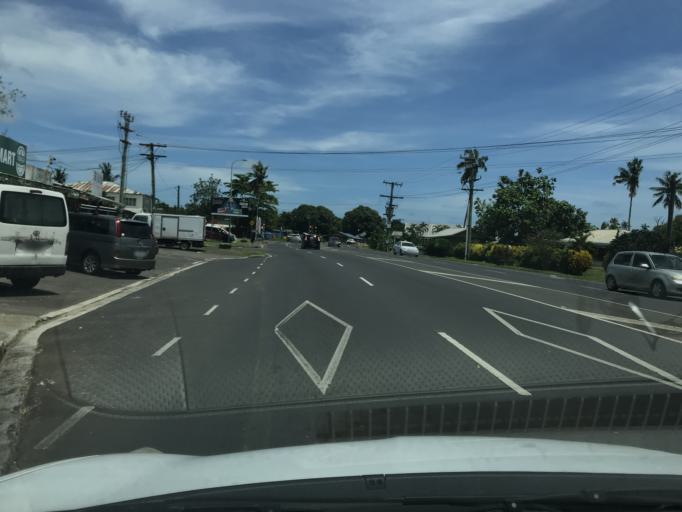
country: WS
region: Tuamasaga
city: Vaiusu
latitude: -13.8338
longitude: -171.7897
